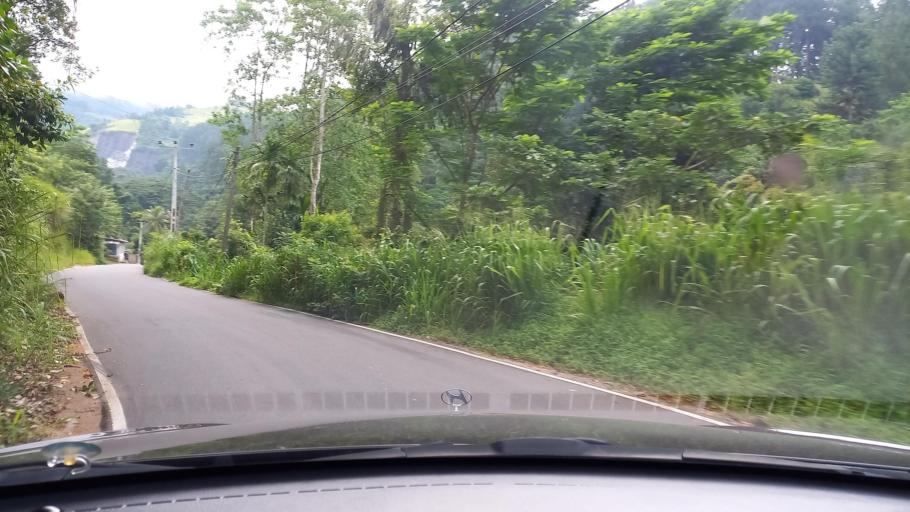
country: LK
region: Central
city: Gampola
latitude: 7.2204
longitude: 80.6100
